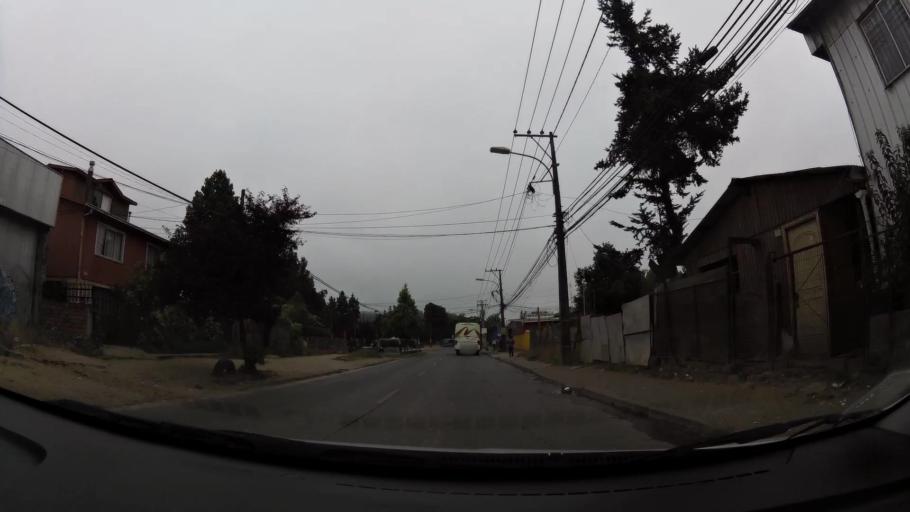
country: CL
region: Biobio
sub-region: Provincia de Concepcion
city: Concepcion
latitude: -36.8217
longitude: -73.0070
